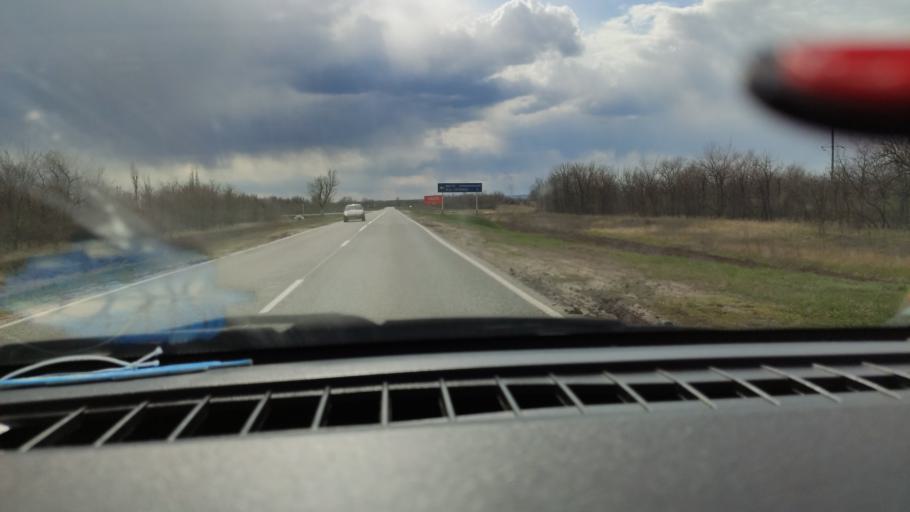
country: RU
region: Saratov
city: Privolzhskiy
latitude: 51.2812
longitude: 45.9586
